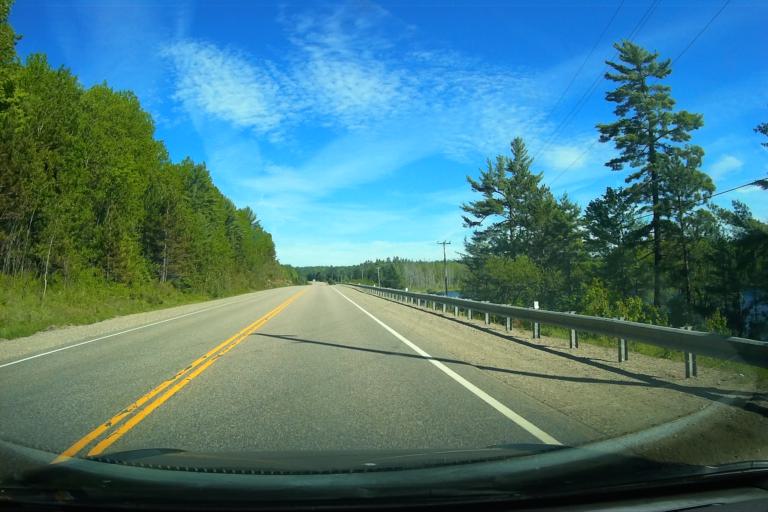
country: CA
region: Ontario
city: Deep River
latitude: 46.1782
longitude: -77.7201
